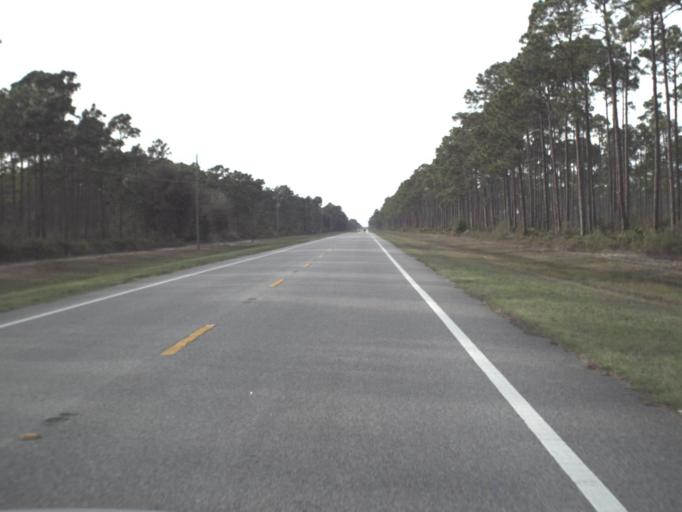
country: US
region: Florida
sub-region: Bay County
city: Tyndall Air Force Base
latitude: 30.0340
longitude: -85.5435
